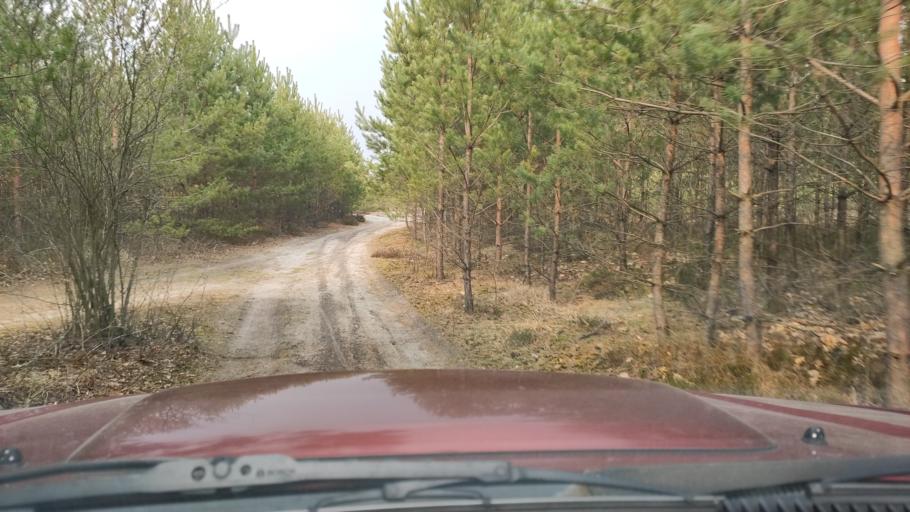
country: PL
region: Masovian Voivodeship
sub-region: Powiat zwolenski
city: Zwolen
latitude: 51.3901
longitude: 21.5712
